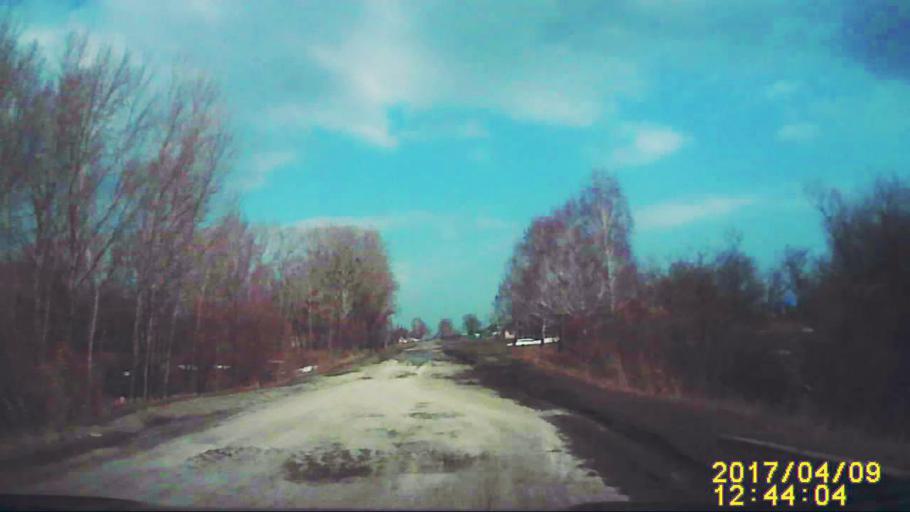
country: RU
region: Ulyanovsk
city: Ignatovka
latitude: 54.0096
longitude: 47.9160
